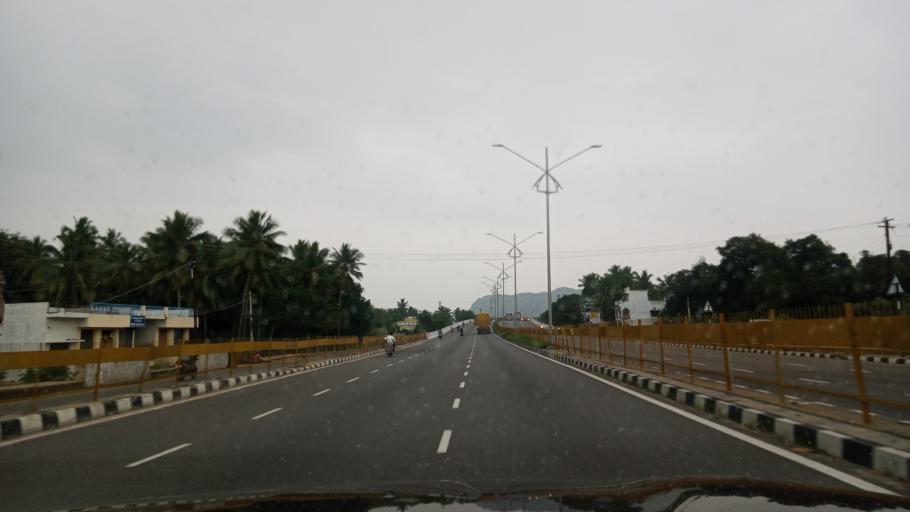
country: IN
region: Tamil Nadu
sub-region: Vellore
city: Katpadi
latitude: 12.9420
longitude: 79.1828
